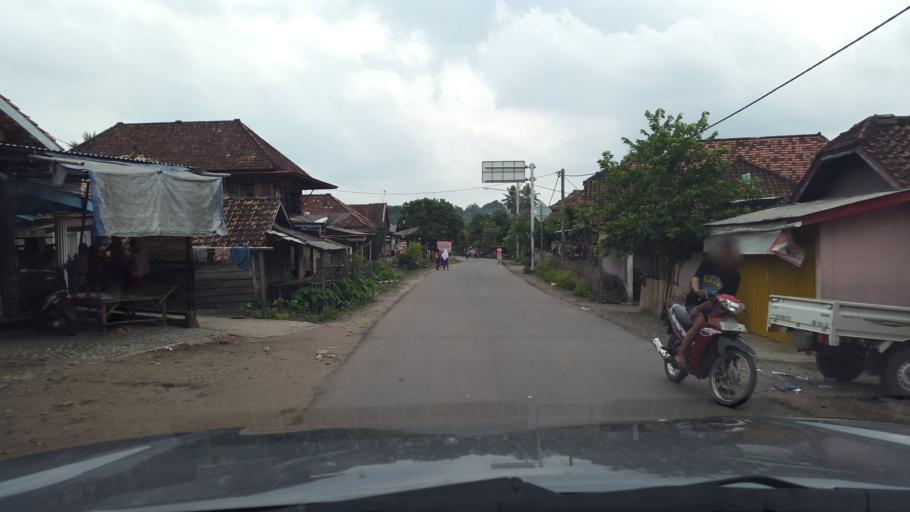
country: ID
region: South Sumatra
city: Gunungmenang
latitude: -3.1787
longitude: 104.0338
